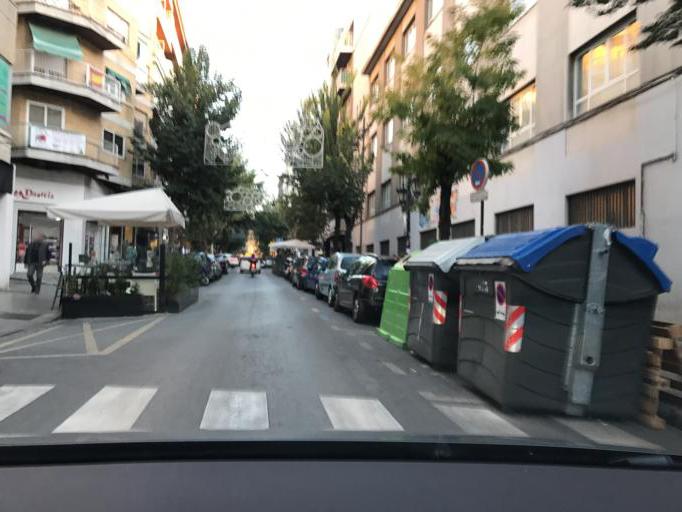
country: ES
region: Andalusia
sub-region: Provincia de Granada
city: Granada
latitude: 37.1767
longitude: -3.6052
